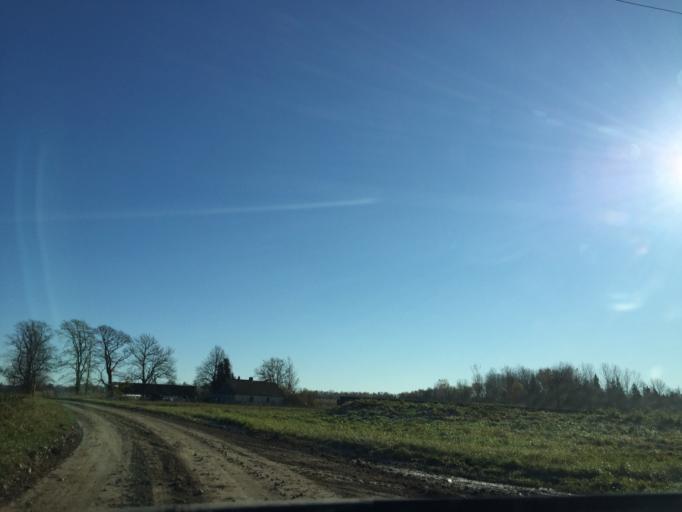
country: LV
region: Skriveri
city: Skriveri
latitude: 56.6546
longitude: 25.1966
